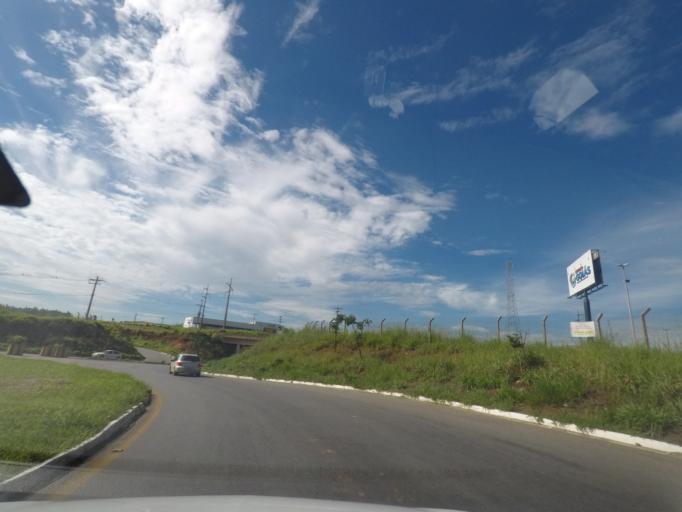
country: BR
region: Goias
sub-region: Aparecida De Goiania
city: Aparecida de Goiania
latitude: -16.7852
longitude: -49.2513
